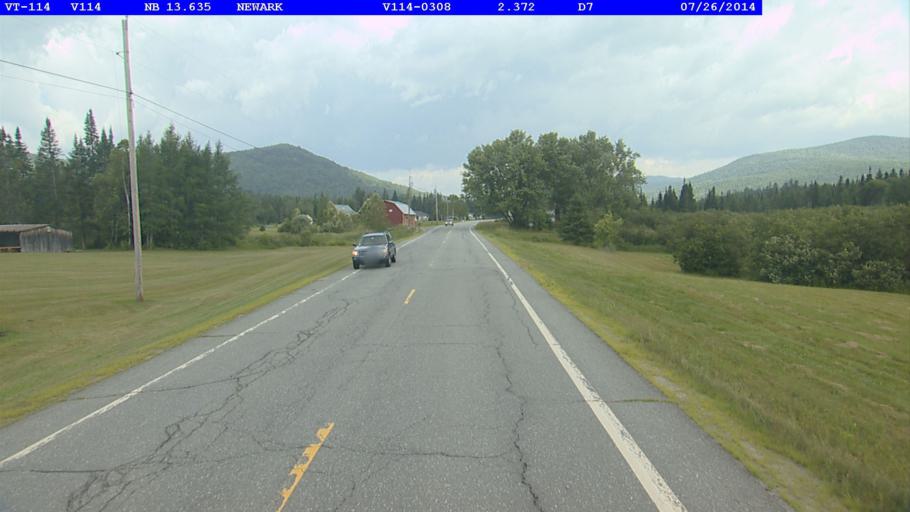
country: US
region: Vermont
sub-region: Caledonia County
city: Lyndonville
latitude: 44.7018
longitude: -71.8712
